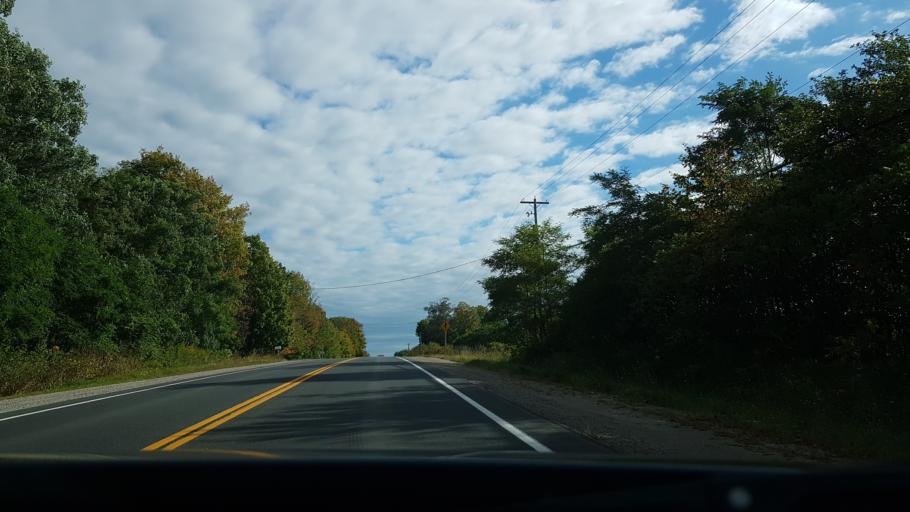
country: CA
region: Ontario
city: Orillia
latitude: 44.6100
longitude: -79.5371
